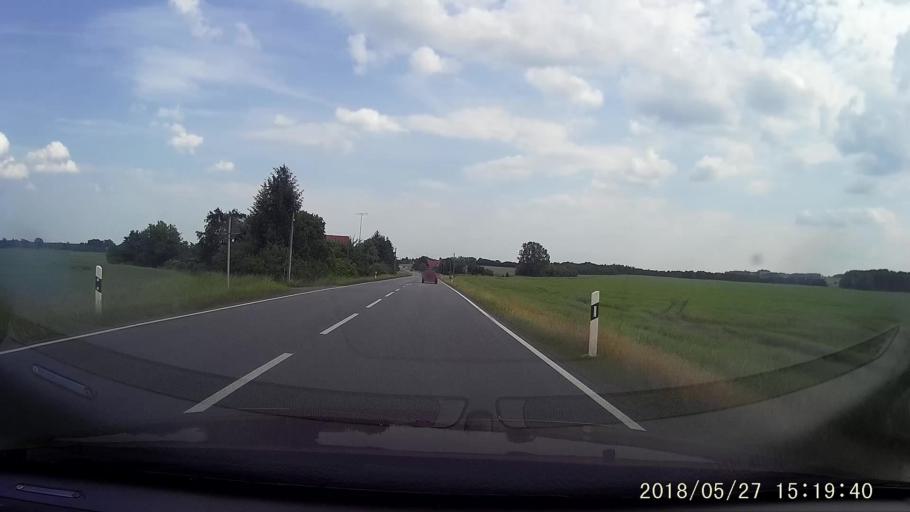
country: DE
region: Saxony
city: Kodersdorf
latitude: 51.2535
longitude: 14.8755
